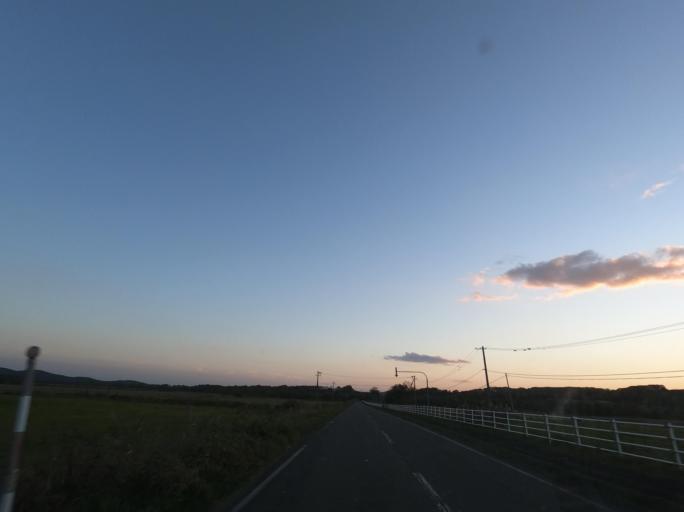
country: JP
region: Hokkaido
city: Kushiro
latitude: 43.2244
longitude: 144.4341
